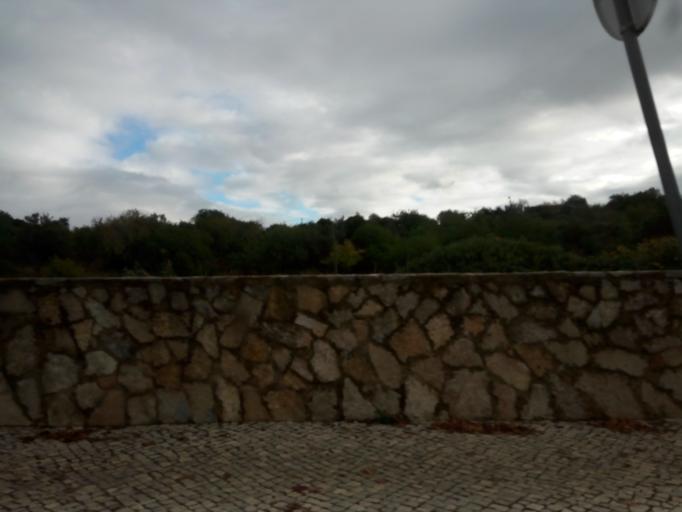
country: PT
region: Faro
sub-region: Loule
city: Loule
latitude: 37.1259
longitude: -8.0170
